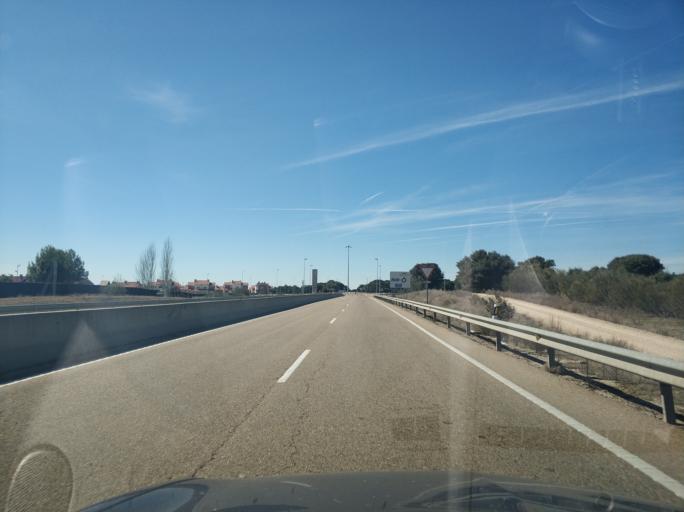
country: ES
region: Castille and Leon
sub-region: Provincia de Valladolid
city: Boecillo
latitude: 41.5359
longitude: -4.7088
